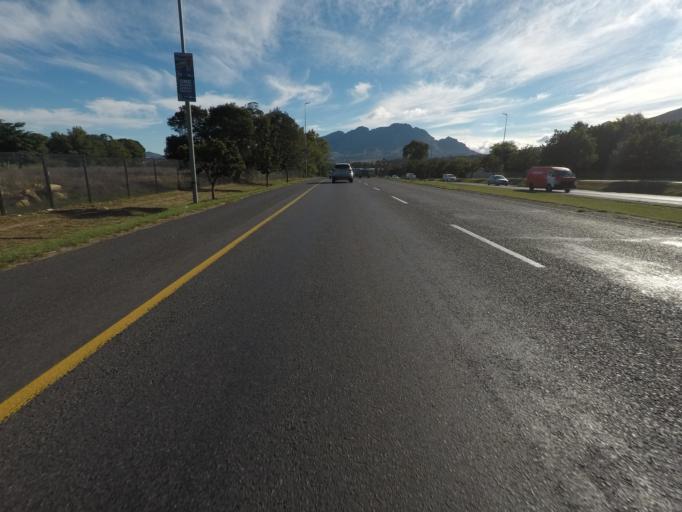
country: ZA
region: Western Cape
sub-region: Cape Winelands District Municipality
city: Stellenbosch
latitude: -33.9615
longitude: 18.8516
